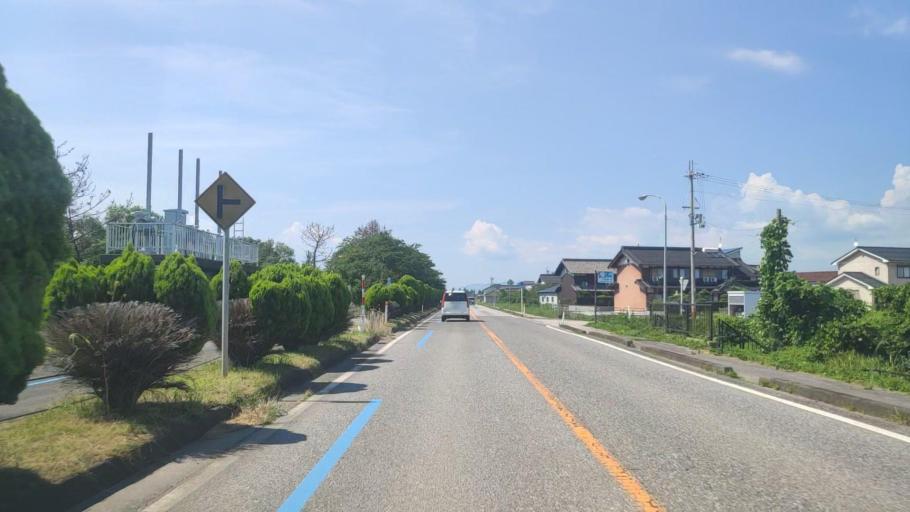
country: JP
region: Shiga Prefecture
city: Nagahama
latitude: 35.4005
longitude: 136.2165
